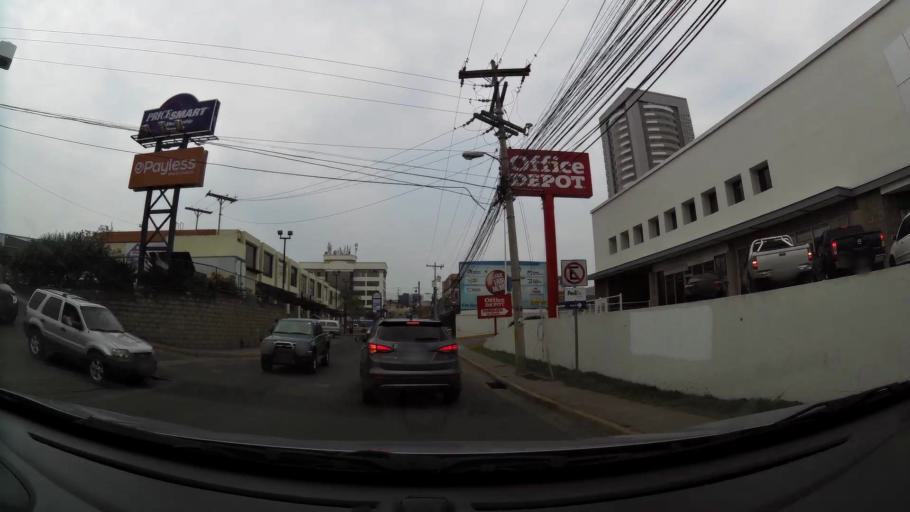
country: HN
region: Francisco Morazan
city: Tegucigalpa
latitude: 14.0874
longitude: -87.1850
